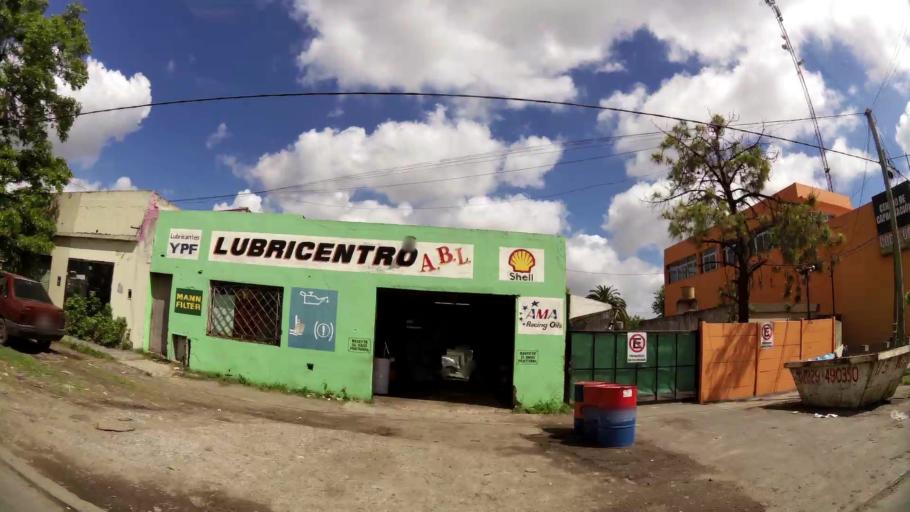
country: AR
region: Buenos Aires
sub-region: Partido de Quilmes
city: Quilmes
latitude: -34.8390
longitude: -58.1880
